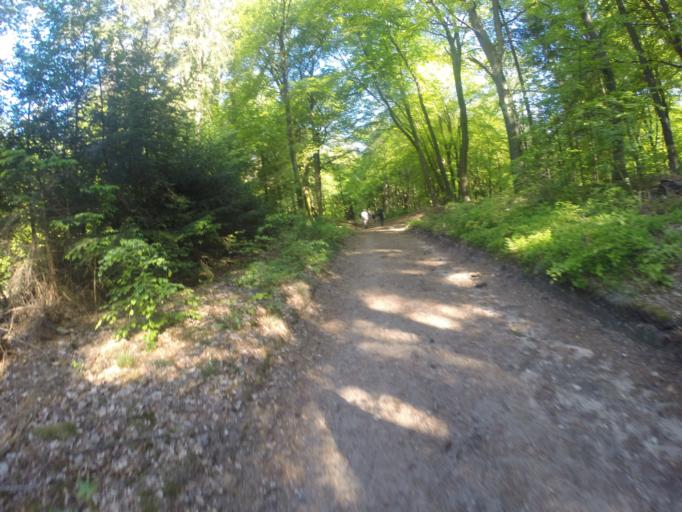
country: NL
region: Gelderland
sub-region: Gemeente Montferland
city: s-Heerenberg
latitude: 51.9047
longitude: 6.2191
